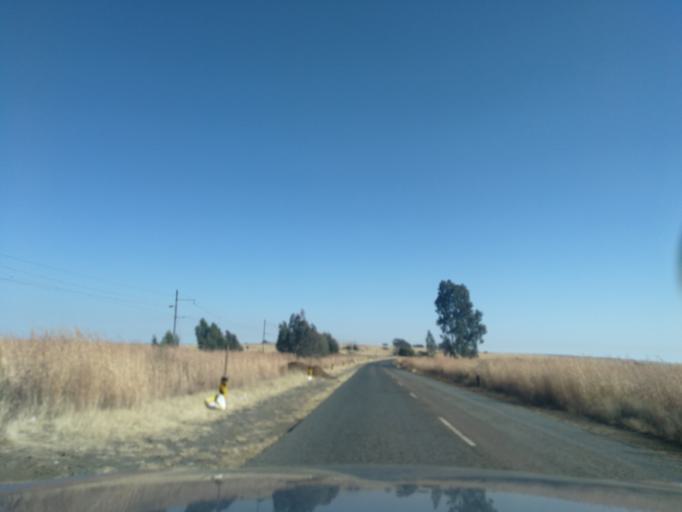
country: ZA
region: Orange Free State
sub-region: Fezile Dabi District Municipality
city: Kroonstad
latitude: -27.8909
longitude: 27.4823
